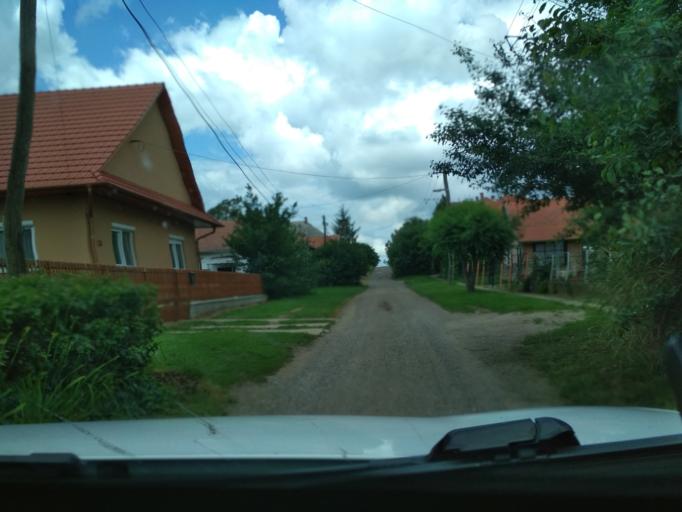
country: HU
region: Jasz-Nagykun-Szolnok
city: Tiszafured
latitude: 47.6087
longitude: 20.7485
